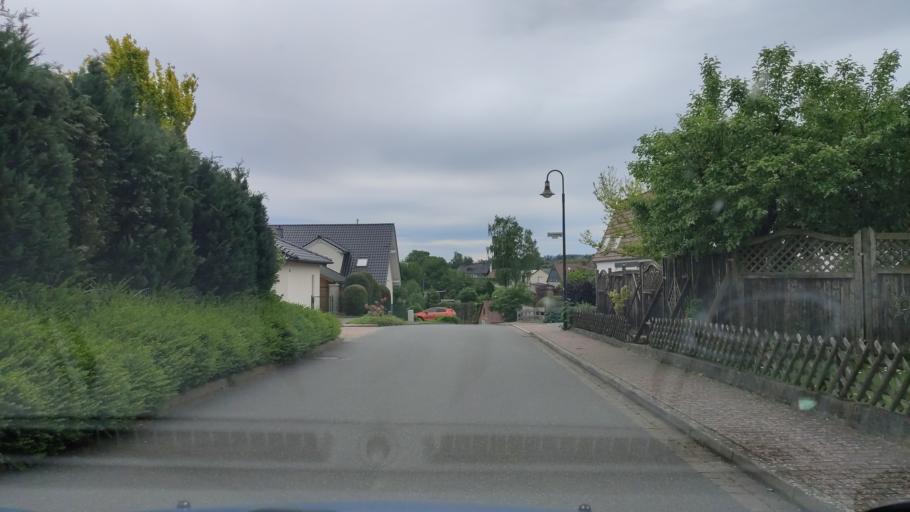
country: DE
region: Lower Saxony
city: Uslar
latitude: 51.6609
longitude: 9.6448
